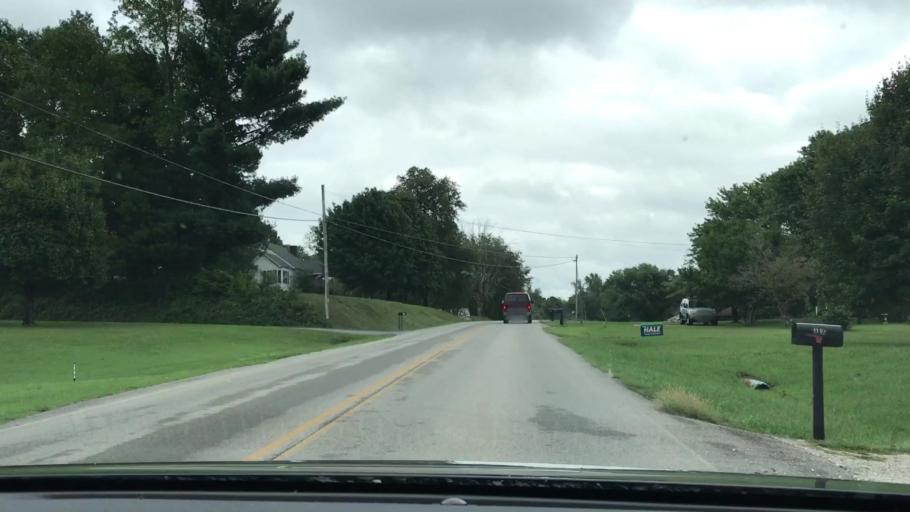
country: US
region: Kentucky
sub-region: Barren County
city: Glasgow
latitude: 36.9641
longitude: -85.8714
